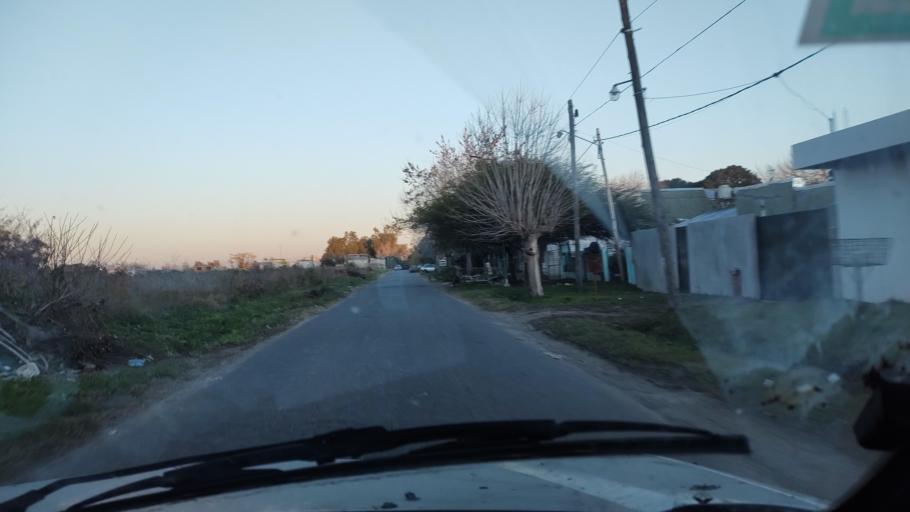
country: AR
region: Buenos Aires
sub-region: Partido de La Plata
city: La Plata
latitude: -34.9086
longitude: -58.0191
